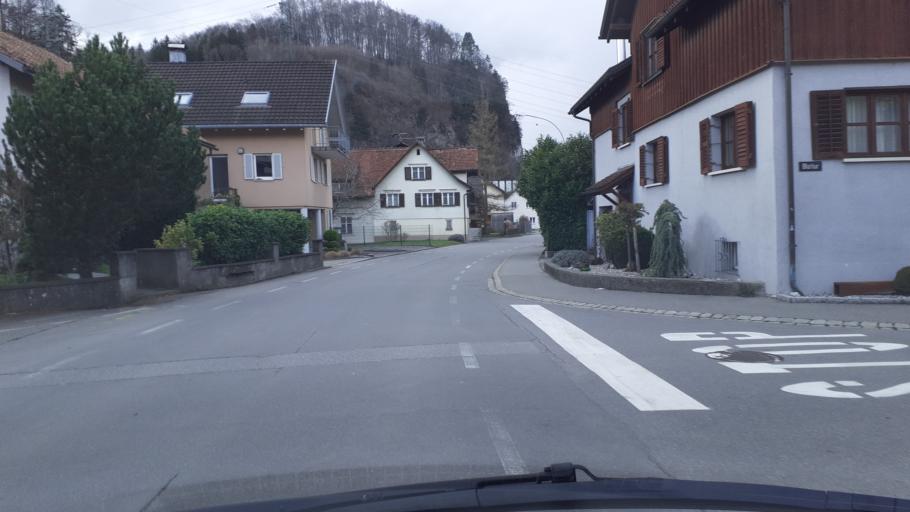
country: AT
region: Vorarlberg
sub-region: Politischer Bezirk Feldkirch
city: Gotzis
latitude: 47.3336
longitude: 9.6321
